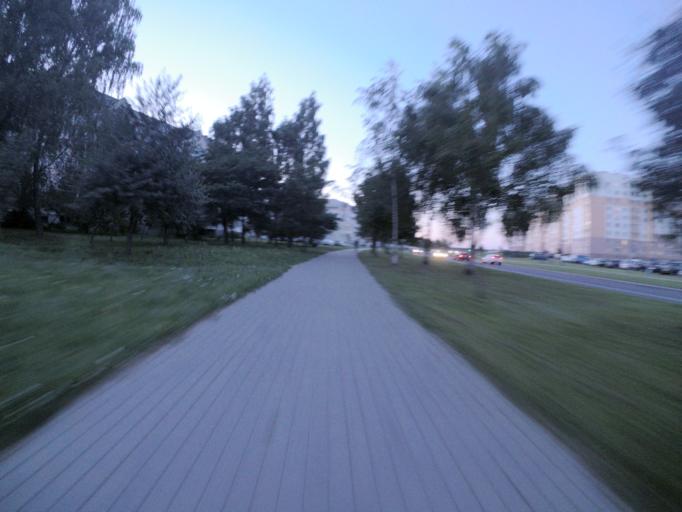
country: BY
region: Grodnenskaya
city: Hrodna
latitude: 53.7114
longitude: 23.8587
